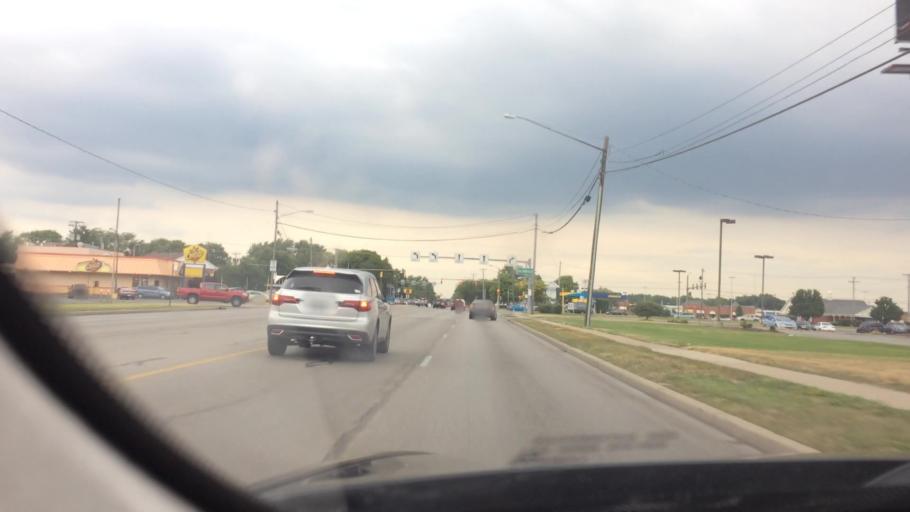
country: US
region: Ohio
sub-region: Wood County
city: Perrysburg
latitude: 41.6107
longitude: -83.6257
